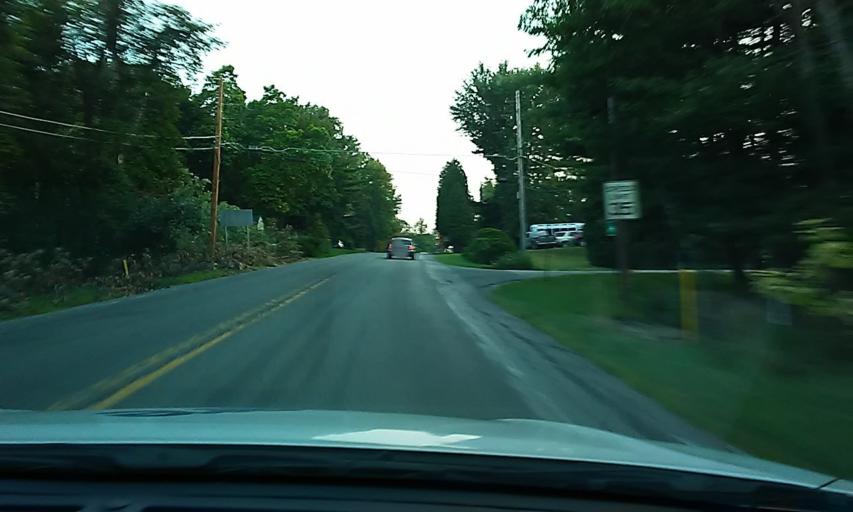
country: US
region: Pennsylvania
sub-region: Clarion County
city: Marianne
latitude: 41.2454
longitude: -79.4209
